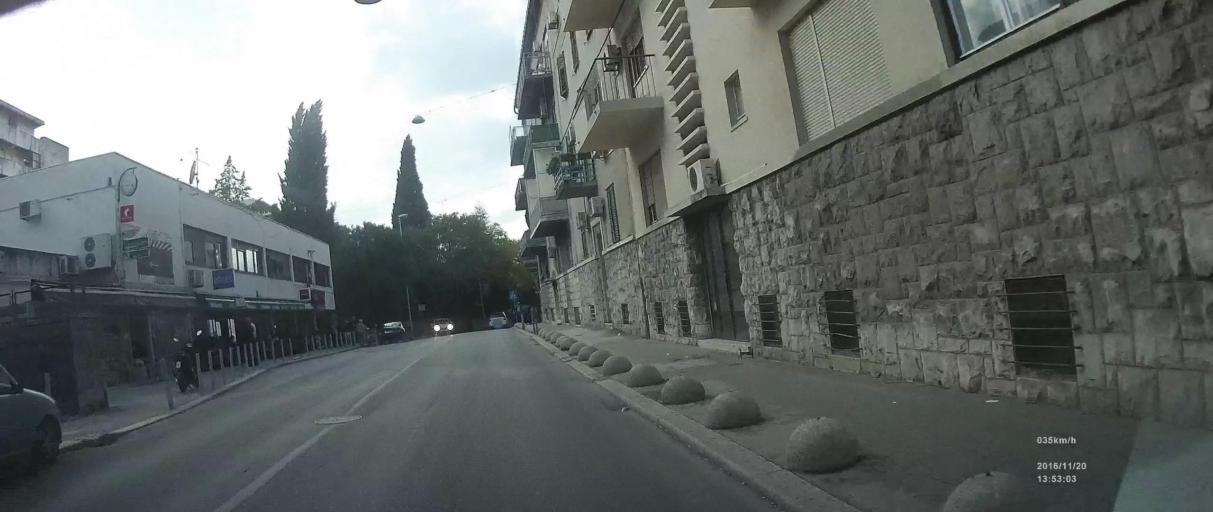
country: HR
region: Splitsko-Dalmatinska
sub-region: Grad Split
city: Split
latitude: 43.5132
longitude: 16.4301
